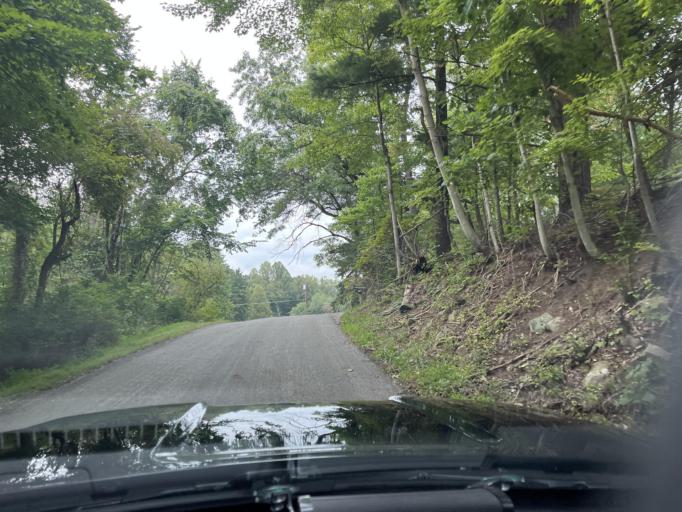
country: US
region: Pennsylvania
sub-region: Fayette County
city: Hopwood
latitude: 39.8662
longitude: -79.6958
